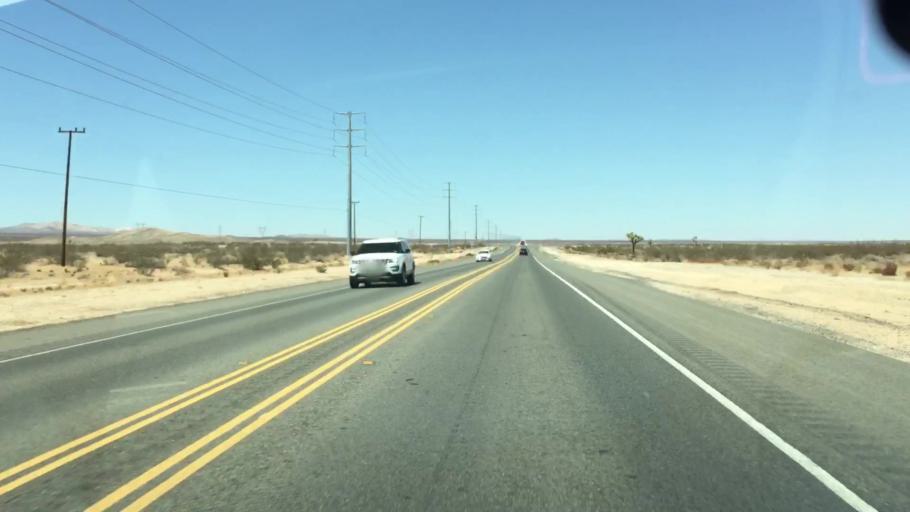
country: US
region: California
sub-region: San Bernardino County
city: Adelanto
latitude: 34.6418
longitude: -117.4335
